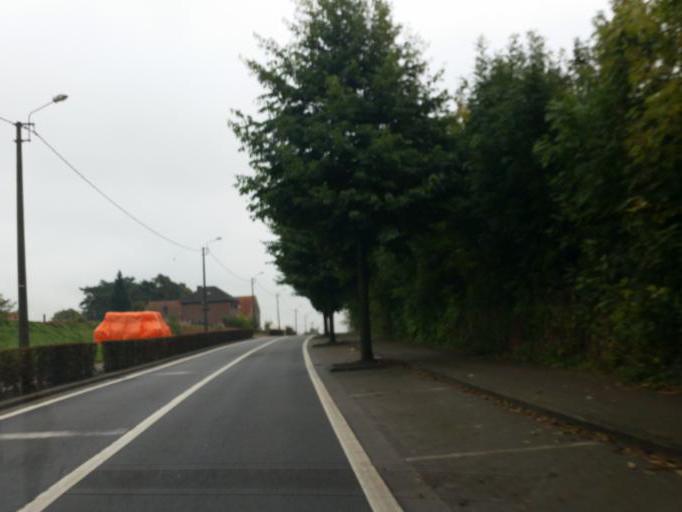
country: BE
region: Flanders
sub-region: Provincie Vlaams-Brabant
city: Sint-Pieters-Leeuw
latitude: 50.7793
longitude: 4.2547
